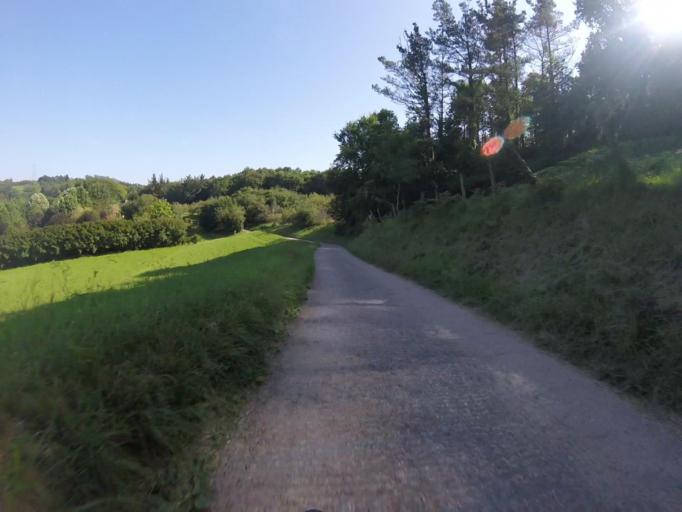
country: ES
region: Basque Country
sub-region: Provincia de Guipuzcoa
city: Astigarraga
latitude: 43.2712
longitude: -1.9336
